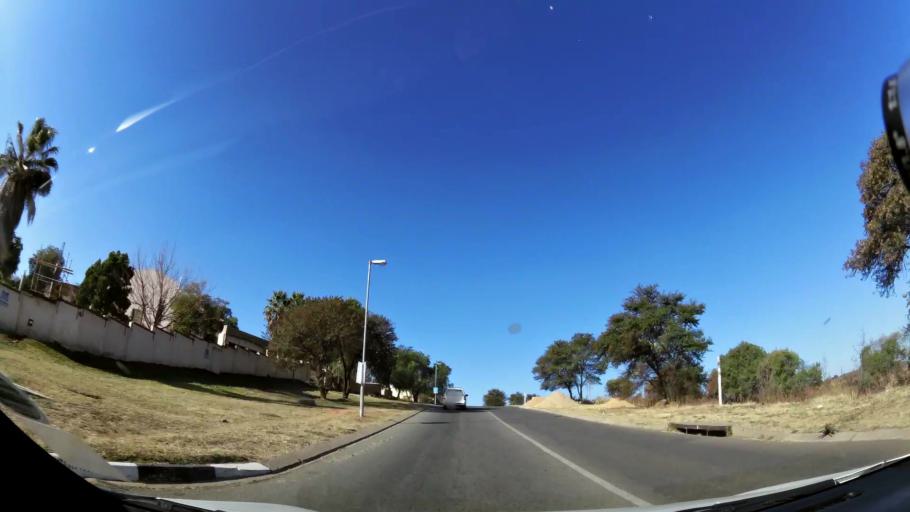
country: ZA
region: Gauteng
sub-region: City of Johannesburg Metropolitan Municipality
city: Johannesburg
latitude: -26.3020
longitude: 28.0564
